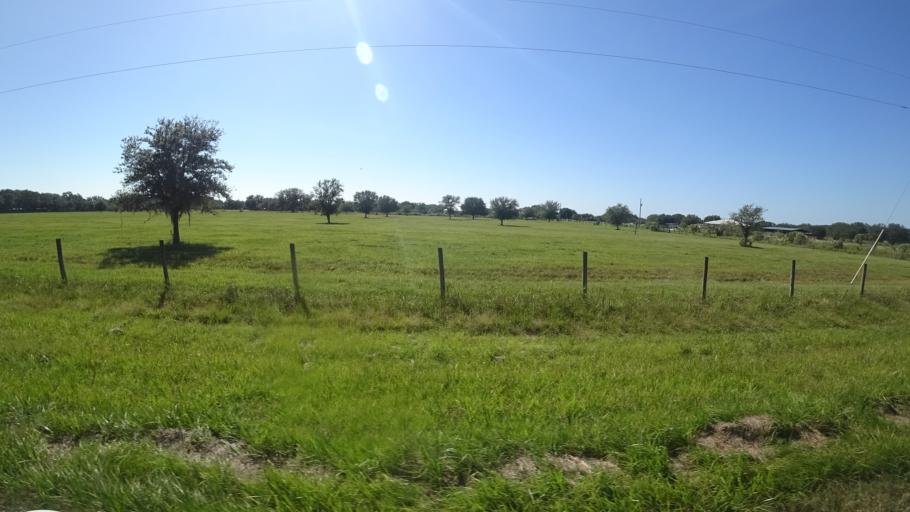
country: US
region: Florida
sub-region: Sarasota County
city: Warm Mineral Springs
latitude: 27.2736
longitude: -82.1494
